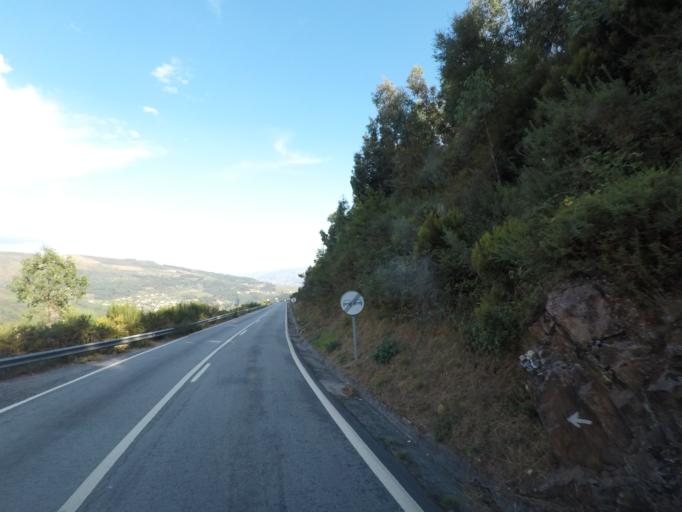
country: PT
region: Porto
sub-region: Baiao
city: Valadares
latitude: 41.1792
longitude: -7.9330
